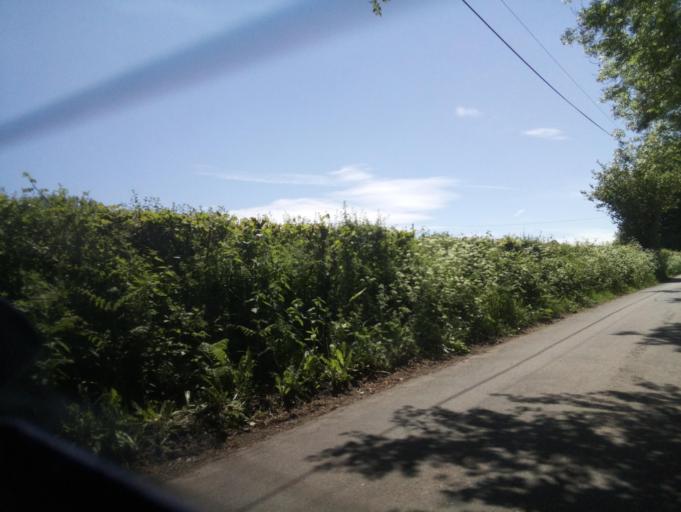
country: GB
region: Wales
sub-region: Monmouthshire
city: Llangwm
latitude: 51.6795
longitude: -2.7654
